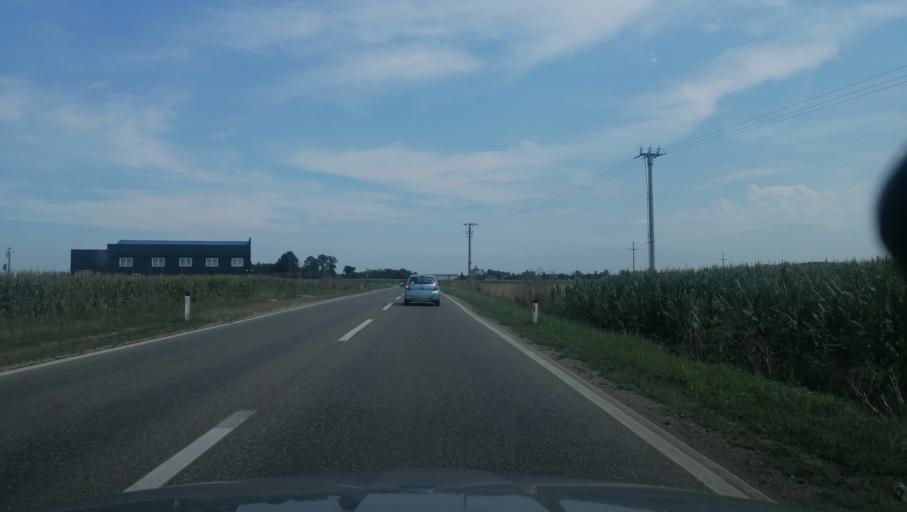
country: BA
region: Republika Srpska
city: Dvorovi
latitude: 44.7875
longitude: 19.2596
